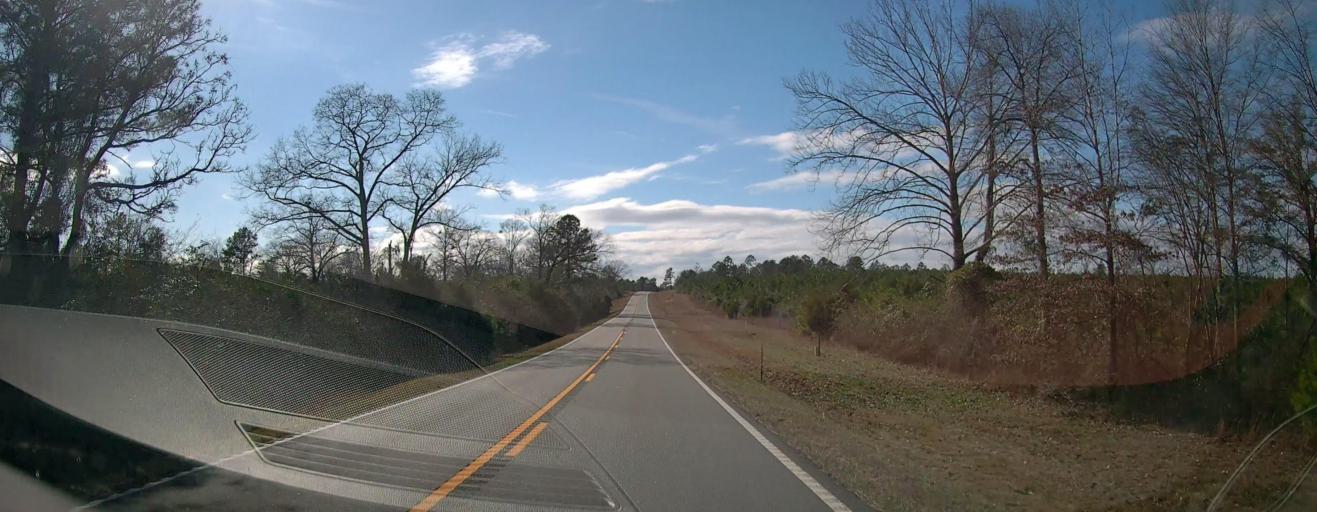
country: US
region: Georgia
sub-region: Taylor County
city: Butler
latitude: 32.4398
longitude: -84.2669
